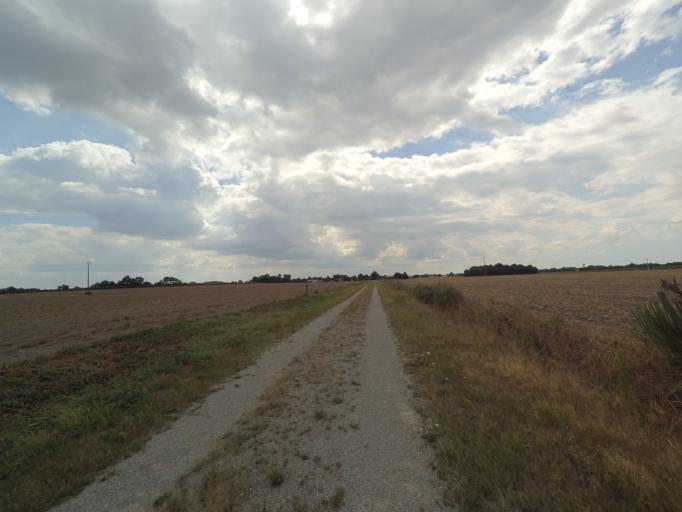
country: FR
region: Pays de la Loire
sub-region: Departement de la Loire-Atlantique
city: Vieillevigne
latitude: 46.9797
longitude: -1.4147
